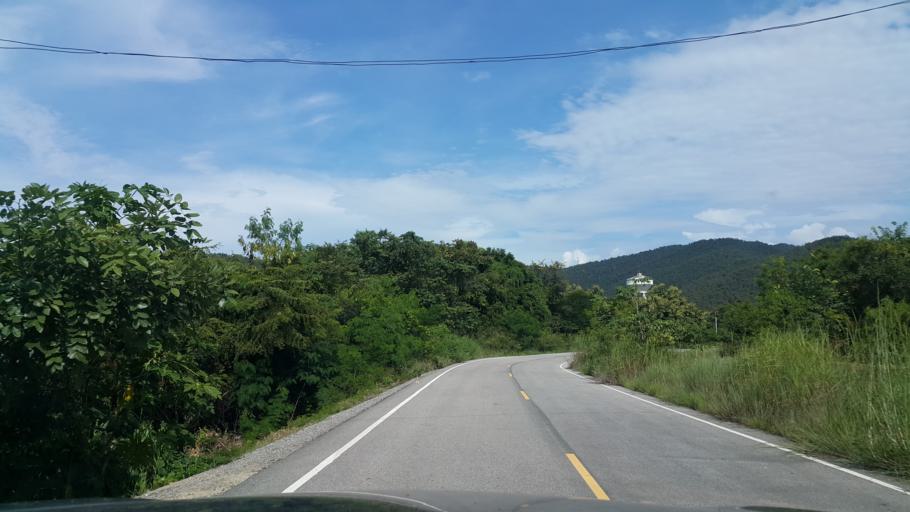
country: TH
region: Chiang Mai
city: Mae On
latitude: 18.8172
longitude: 99.1824
